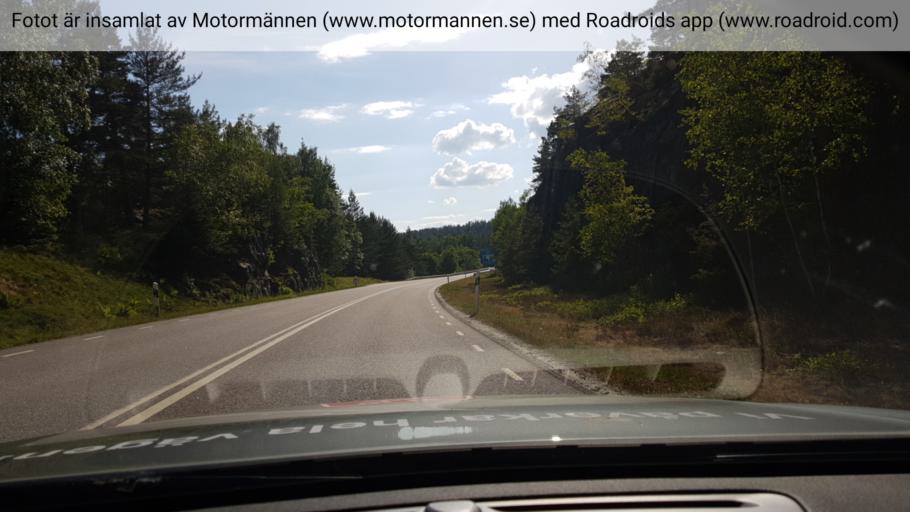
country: SE
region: Vaestra Goetaland
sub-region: Karlsborgs Kommun
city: Karlsborg
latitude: 58.6347
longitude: 14.5514
